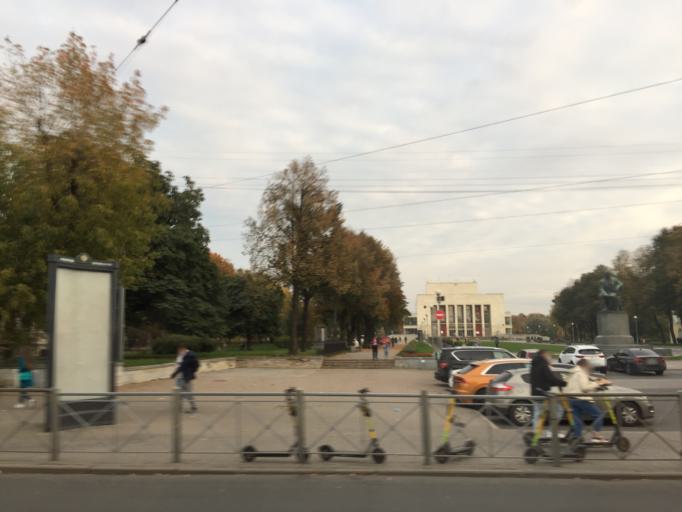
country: RU
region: St.-Petersburg
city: Saint Petersburg
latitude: 59.9219
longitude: 30.3321
